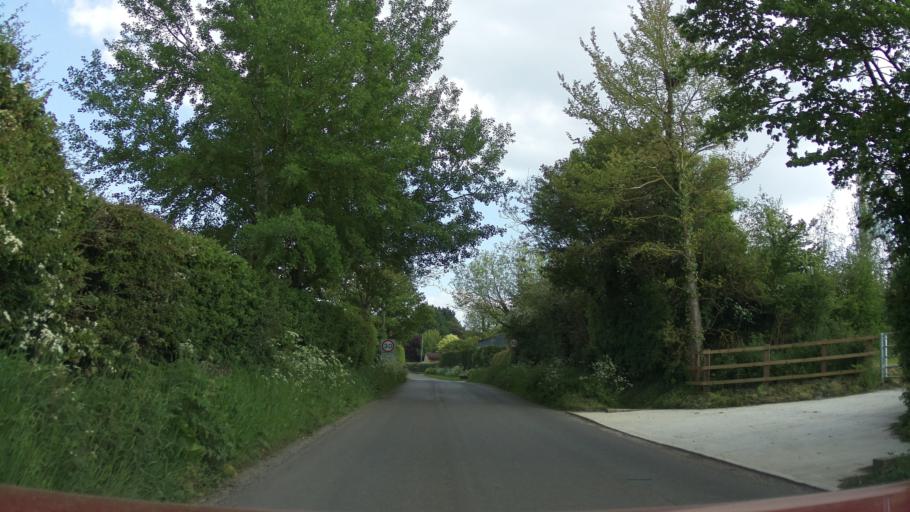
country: GB
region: England
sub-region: Wiltshire
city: Malmesbury
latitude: 51.5433
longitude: -2.0841
